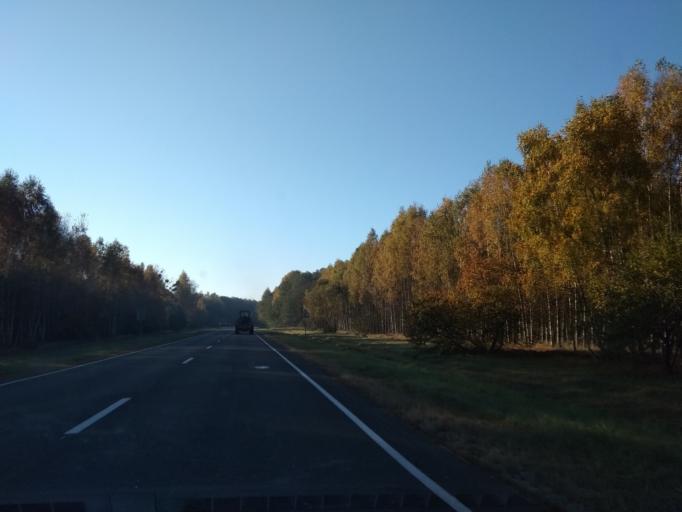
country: BY
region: Brest
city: Kobryn
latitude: 52.0696
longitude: 24.2836
